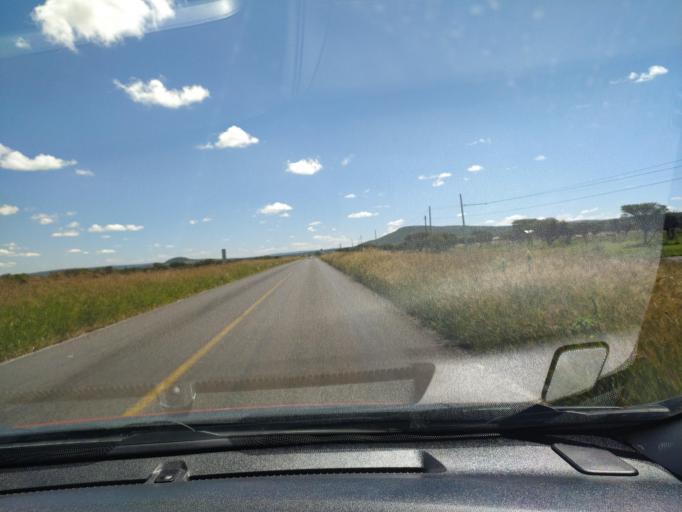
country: MX
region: Jalisco
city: San Miguel el Alto
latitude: 21.0172
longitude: -102.4948
